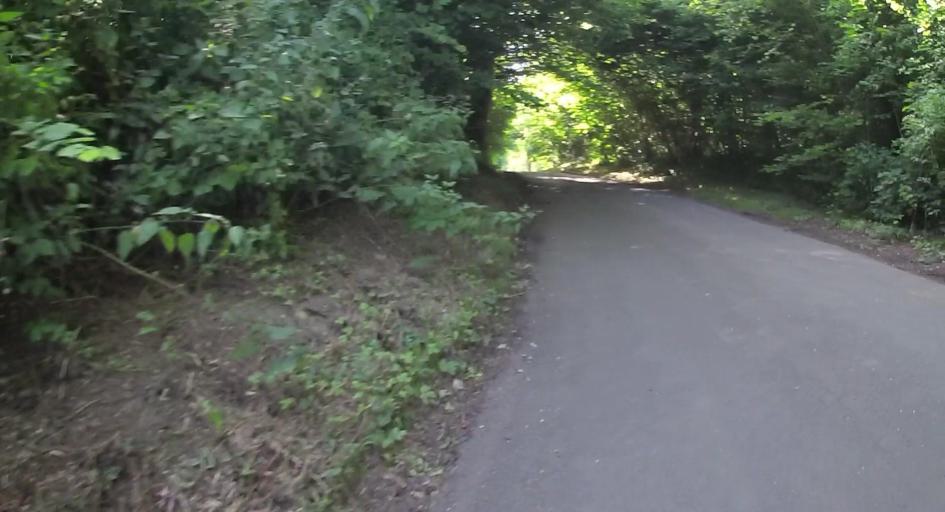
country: GB
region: England
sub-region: Hampshire
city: Long Sutton
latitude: 51.1857
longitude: -0.9349
